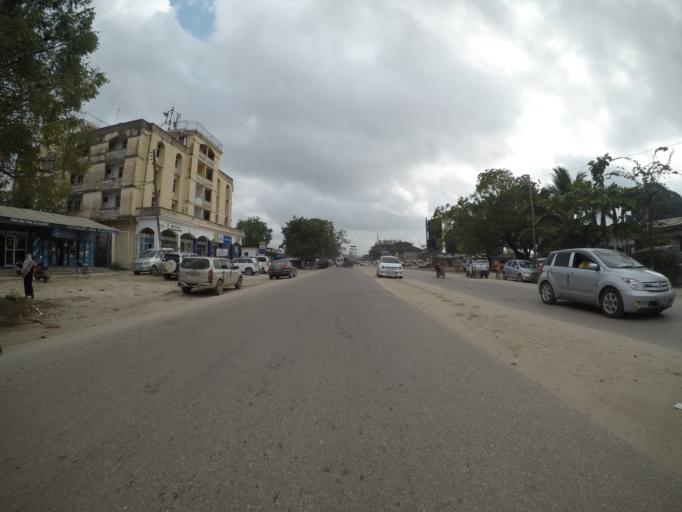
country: TZ
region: Zanzibar Urban/West
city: Zanzibar
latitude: -6.1775
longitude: 39.2223
